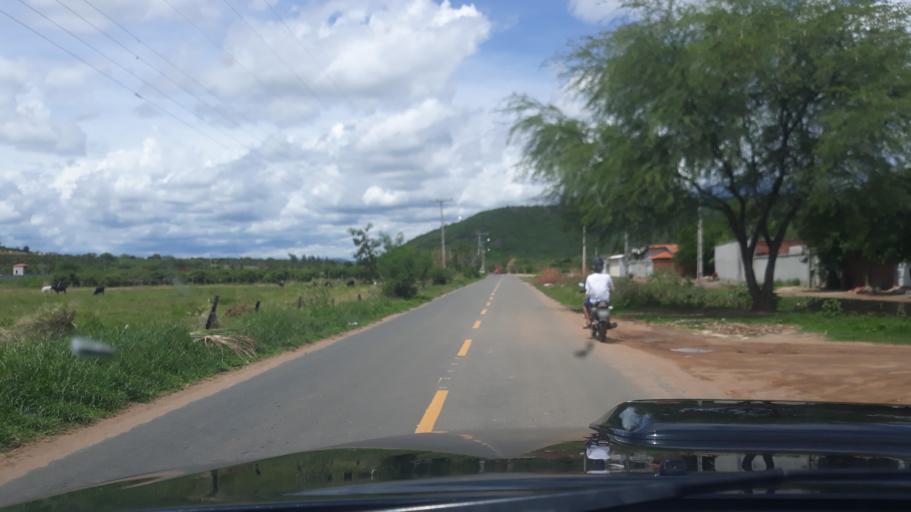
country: BR
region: Bahia
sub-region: Guanambi
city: Guanambi
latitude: -14.2819
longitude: -42.7136
